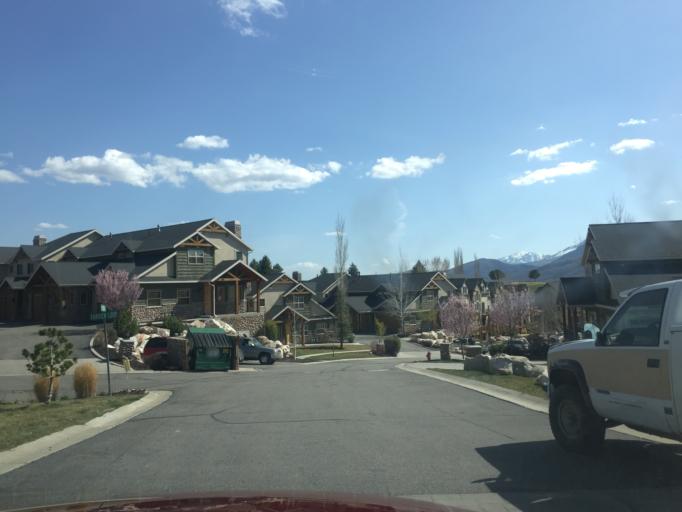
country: US
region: Utah
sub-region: Weber County
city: Wolf Creek
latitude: 41.3254
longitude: -111.8237
